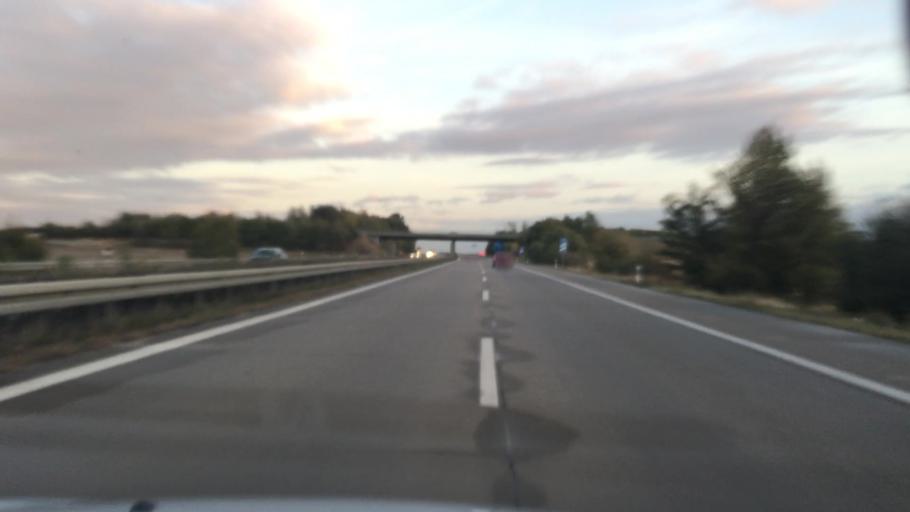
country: DE
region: Saxony
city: Mutzschen
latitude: 51.2450
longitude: 12.8528
